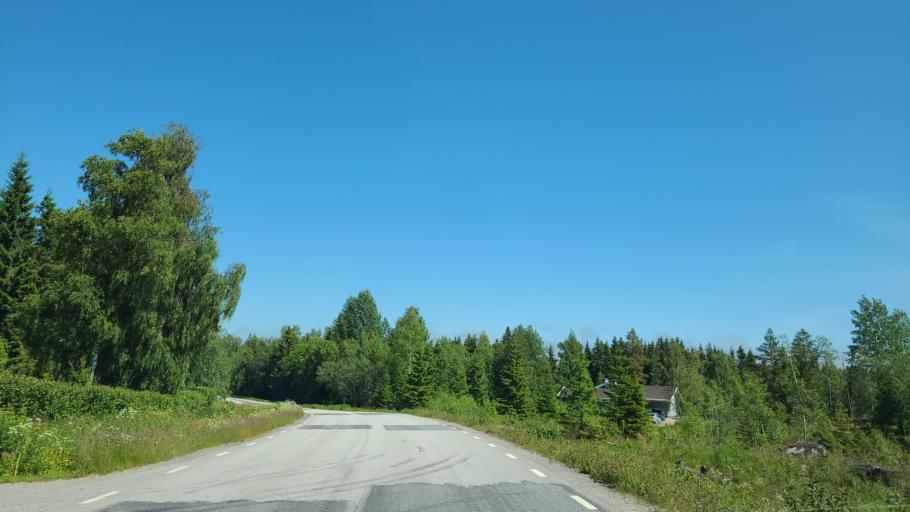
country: SE
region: Vaesternorrland
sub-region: OErnskoeldsviks Kommun
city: Husum
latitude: 63.3905
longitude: 19.2118
